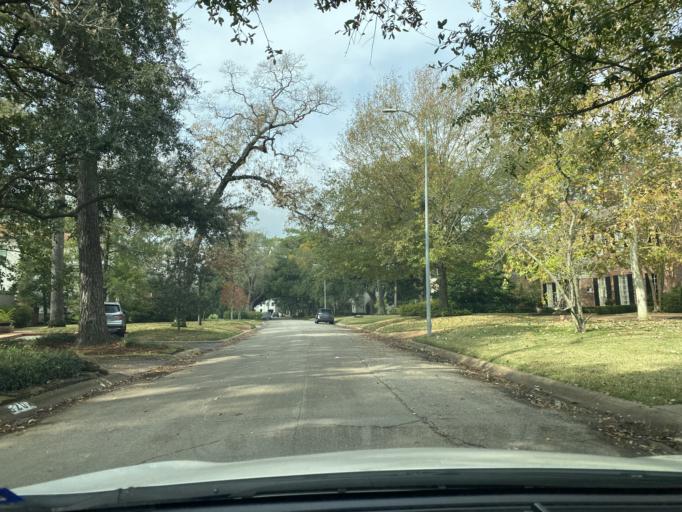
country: US
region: Texas
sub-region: Harris County
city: Hunters Creek Village
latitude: 29.7653
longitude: -95.4682
